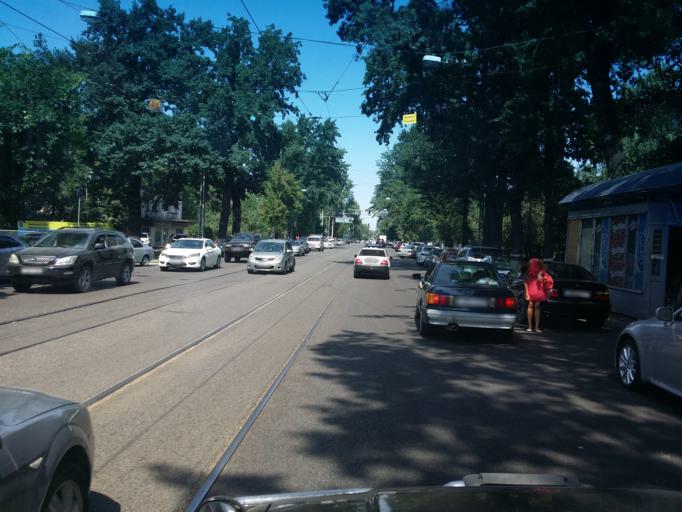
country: KZ
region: Almaty Qalasy
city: Almaty
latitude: 43.2537
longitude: 76.9257
